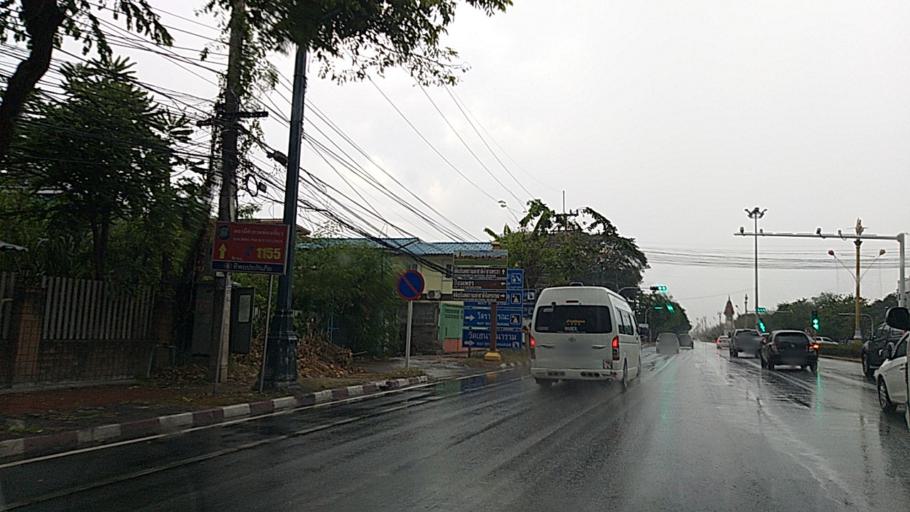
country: TH
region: Phra Nakhon Si Ayutthaya
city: Phra Nakhon Si Ayutthaya
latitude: 14.3513
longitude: 100.5765
